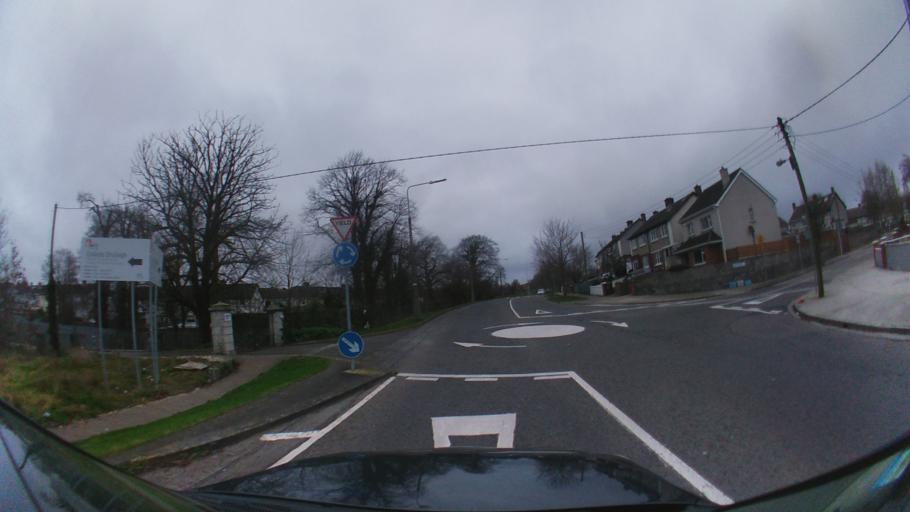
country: IE
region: Leinster
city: Raheny
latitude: 53.3877
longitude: -6.1899
